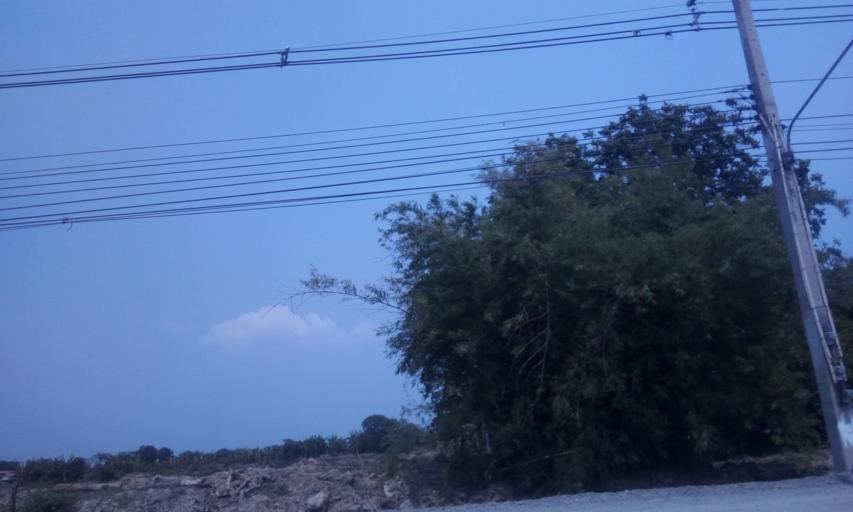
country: TH
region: Chachoengsao
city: Ban Pho
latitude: 13.5544
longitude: 101.1385
